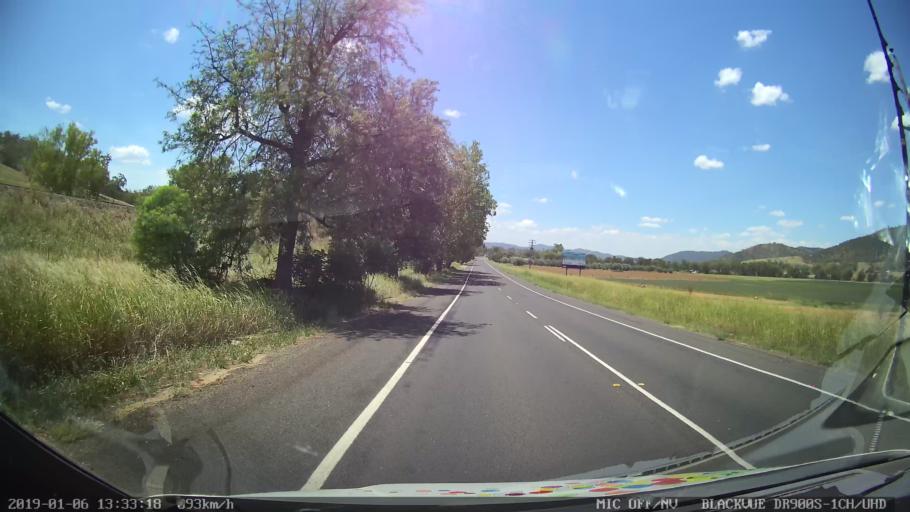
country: AU
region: New South Wales
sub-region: Tamworth Municipality
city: Kootingal
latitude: -31.1005
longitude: 151.0044
